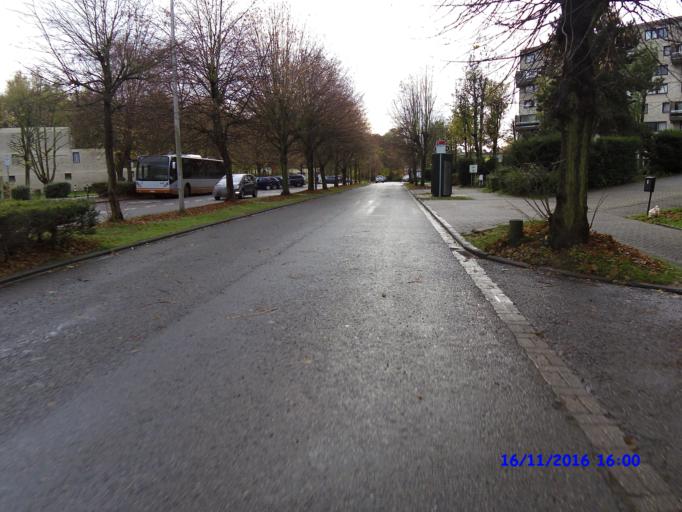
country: BE
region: Flanders
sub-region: Provincie Vlaams-Brabant
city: Diegem
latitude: 50.8536
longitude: 4.4250
